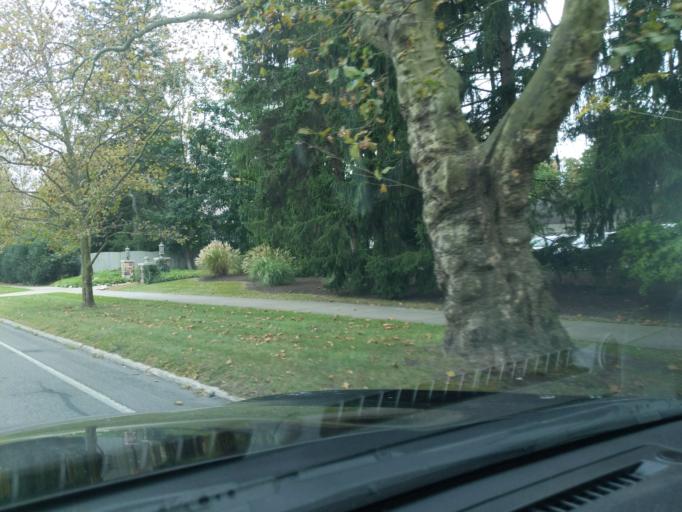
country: US
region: Pennsylvania
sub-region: Blair County
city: Lakemont
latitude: 40.4918
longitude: -78.4064
